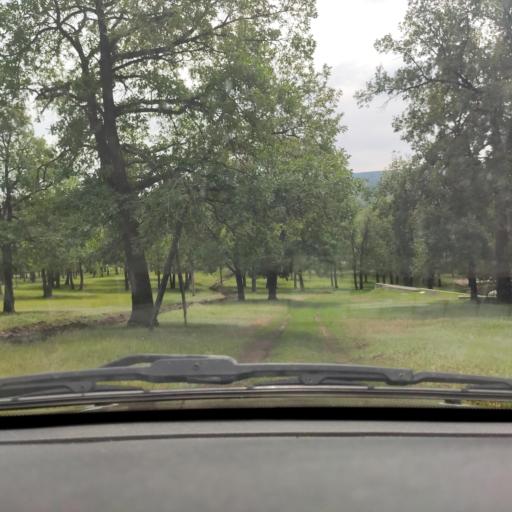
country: RU
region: Samara
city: Zhigulevsk
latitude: 53.4720
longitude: 49.6199
